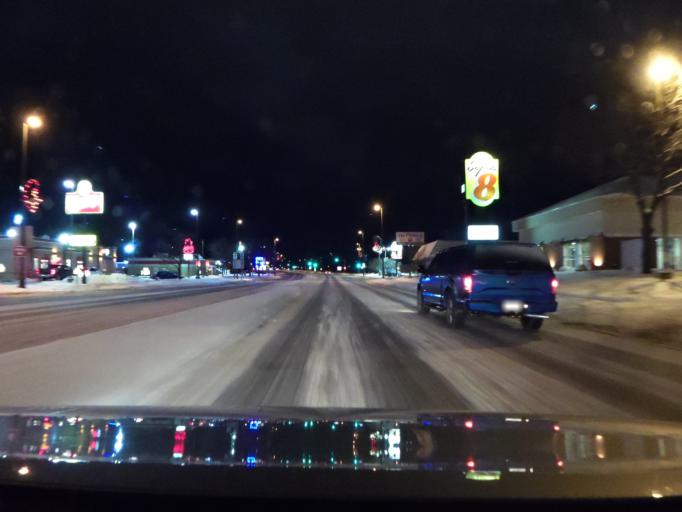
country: US
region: Wisconsin
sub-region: Dunn County
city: Menomonie
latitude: 44.9012
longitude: -91.9320
